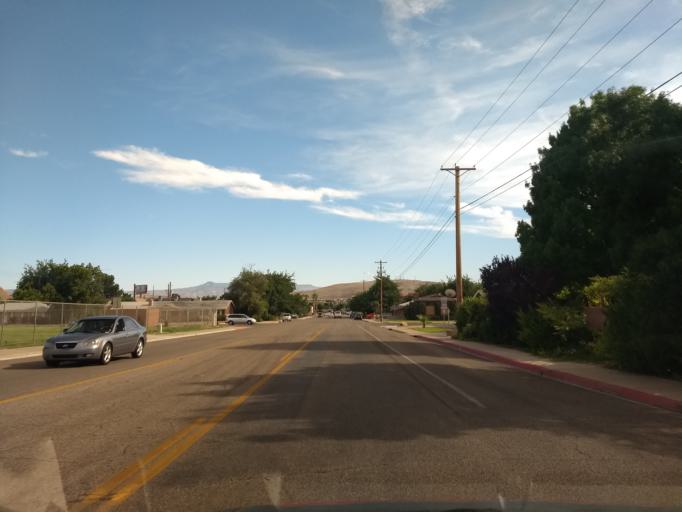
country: US
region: Utah
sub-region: Washington County
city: Saint George
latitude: 37.0988
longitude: -113.5686
